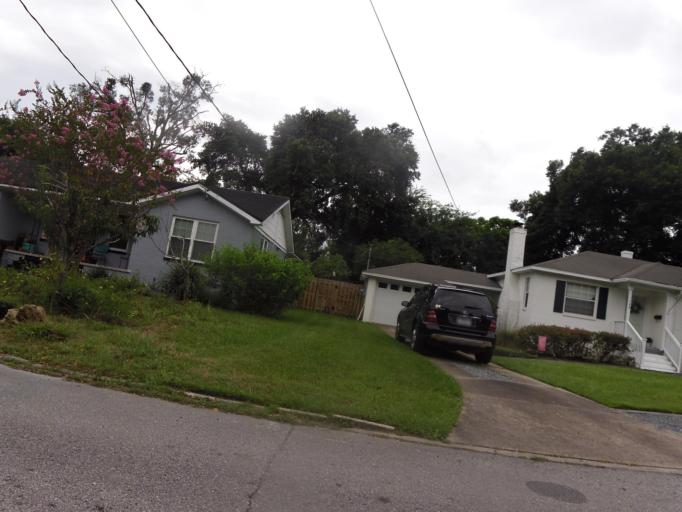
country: US
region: Florida
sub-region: Duval County
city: Jacksonville
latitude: 30.2762
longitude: -81.6524
